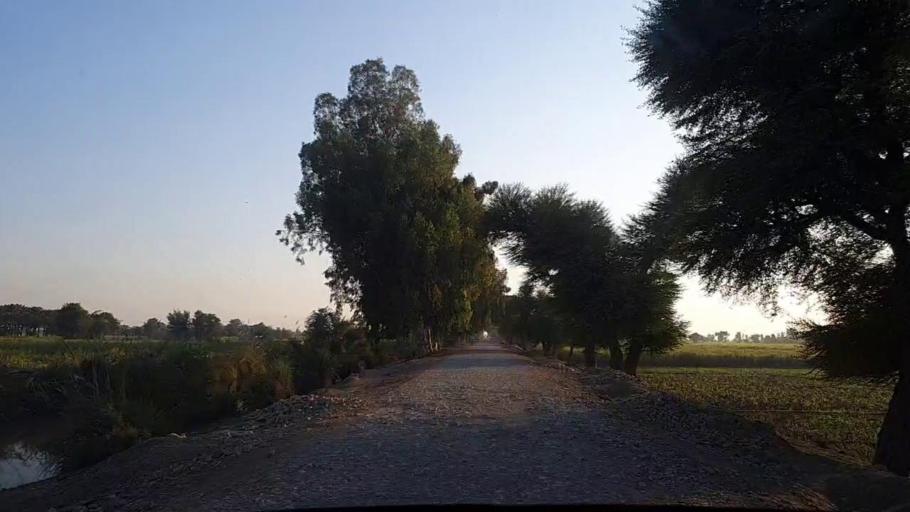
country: PK
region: Sindh
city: Sobhadero
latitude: 27.3833
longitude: 68.3816
